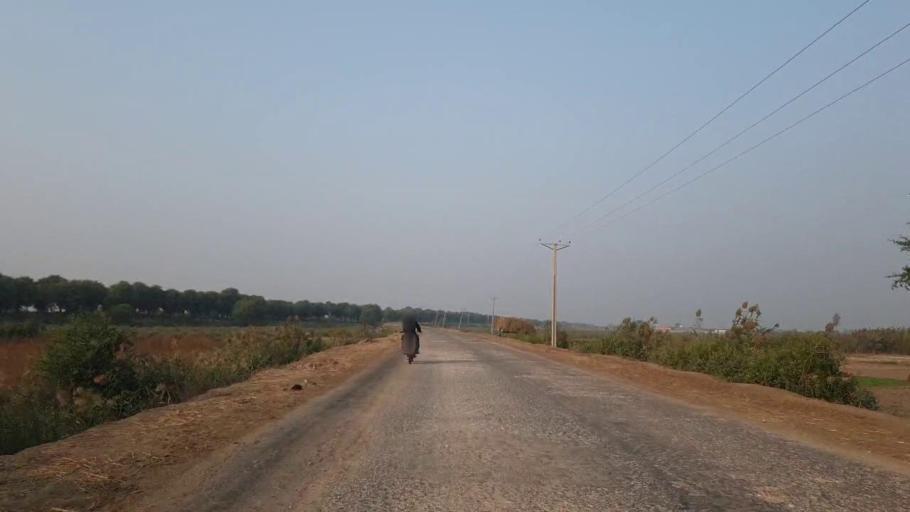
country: PK
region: Sindh
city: Tando Muhammad Khan
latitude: 25.1159
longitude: 68.4280
